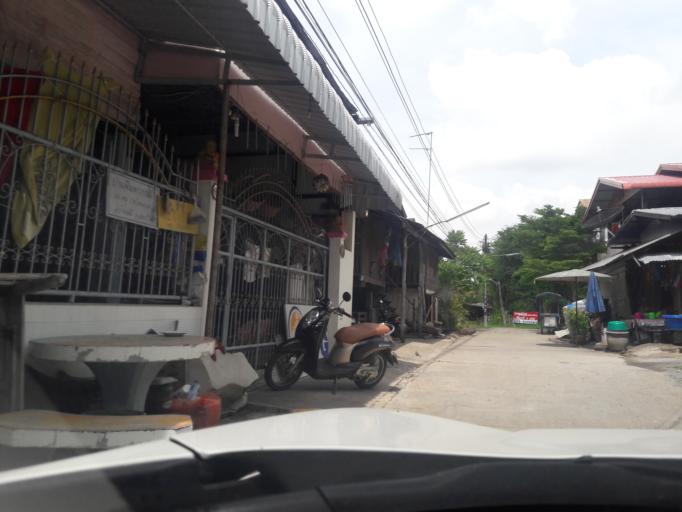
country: TH
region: Lop Buri
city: Ban Mi
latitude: 15.0445
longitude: 100.5465
